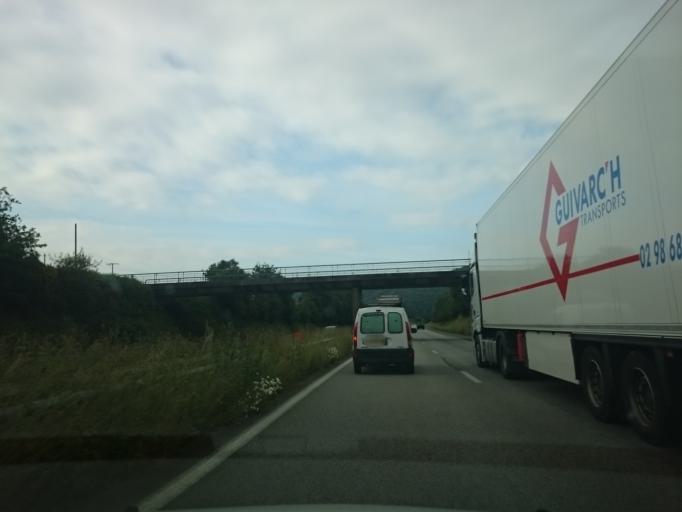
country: FR
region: Brittany
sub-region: Departement du Finistere
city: Chateaulin
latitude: 48.1904
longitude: -4.0455
